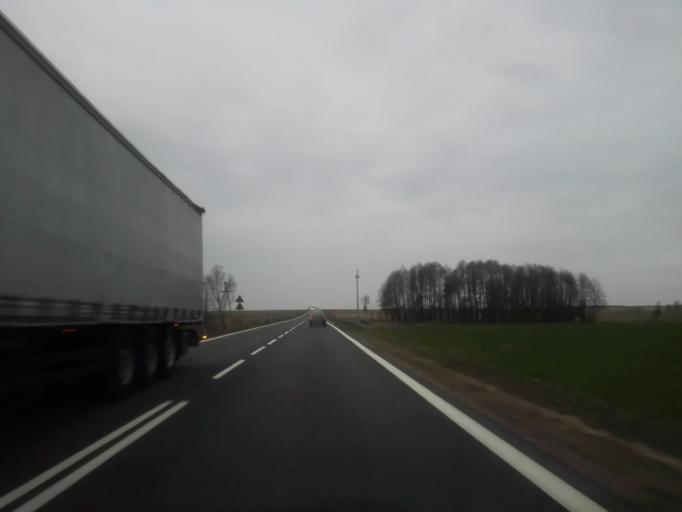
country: PL
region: Podlasie
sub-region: Powiat kolnenski
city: Stawiski
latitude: 53.4180
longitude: 22.1651
